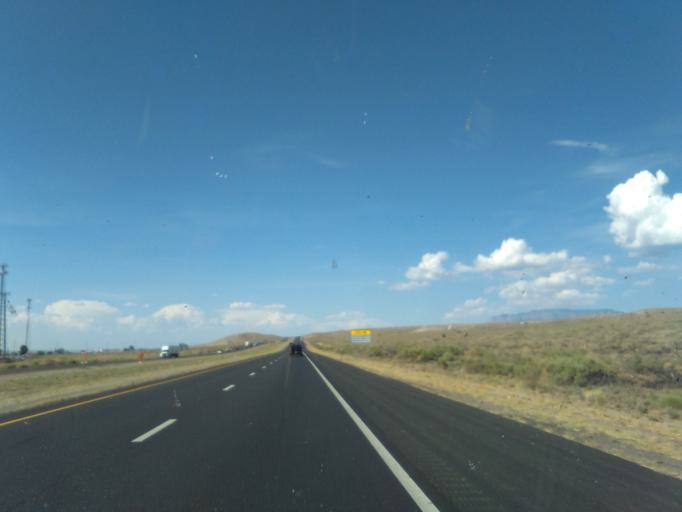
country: US
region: New Mexico
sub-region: Bernalillo County
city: South Valley
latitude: 34.9659
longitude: -106.6564
